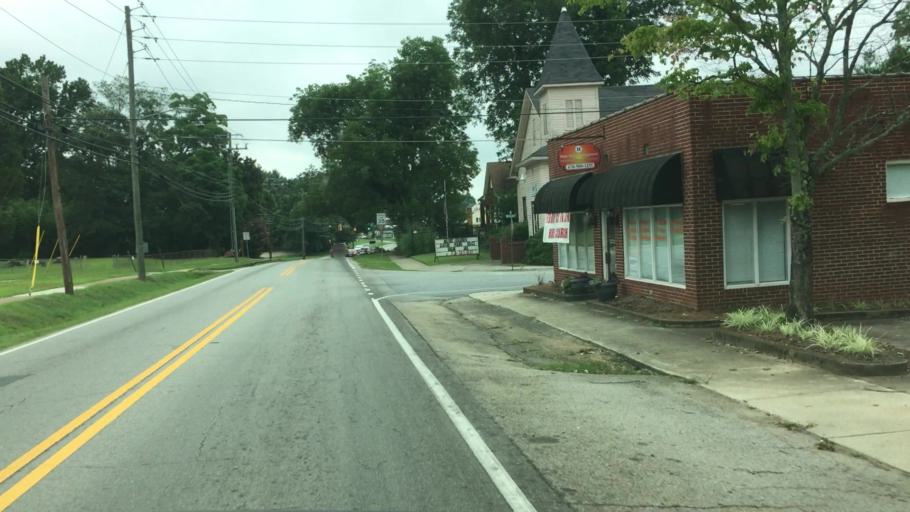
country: US
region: Georgia
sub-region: Barrow County
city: Winder
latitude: 33.9942
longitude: -83.7249
